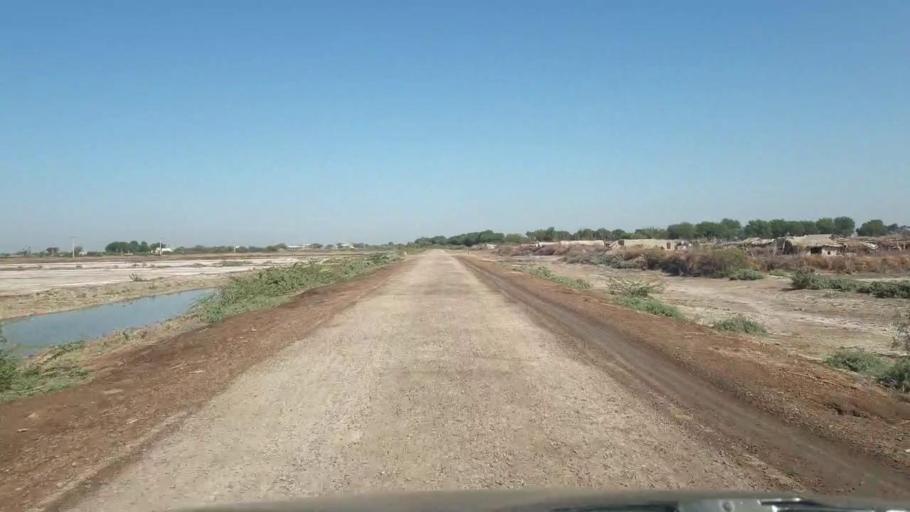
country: PK
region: Sindh
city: Umarkot
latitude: 25.3833
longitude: 69.6737
